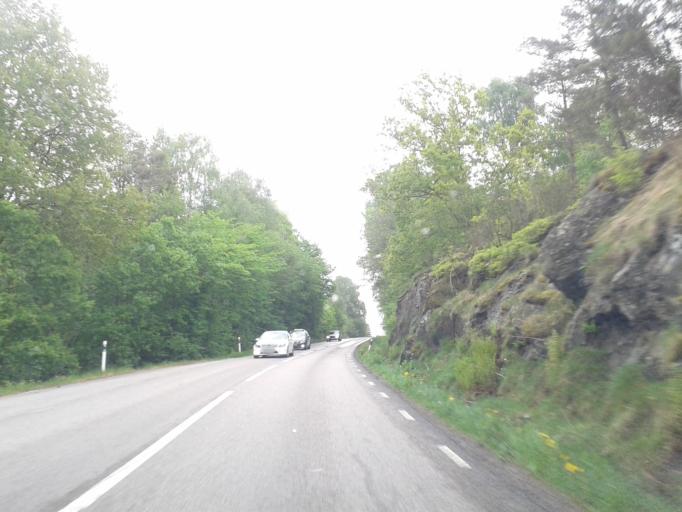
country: SE
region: Vaestra Goetaland
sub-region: Kungalvs Kommun
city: Kode
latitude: 57.8938
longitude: 11.8510
